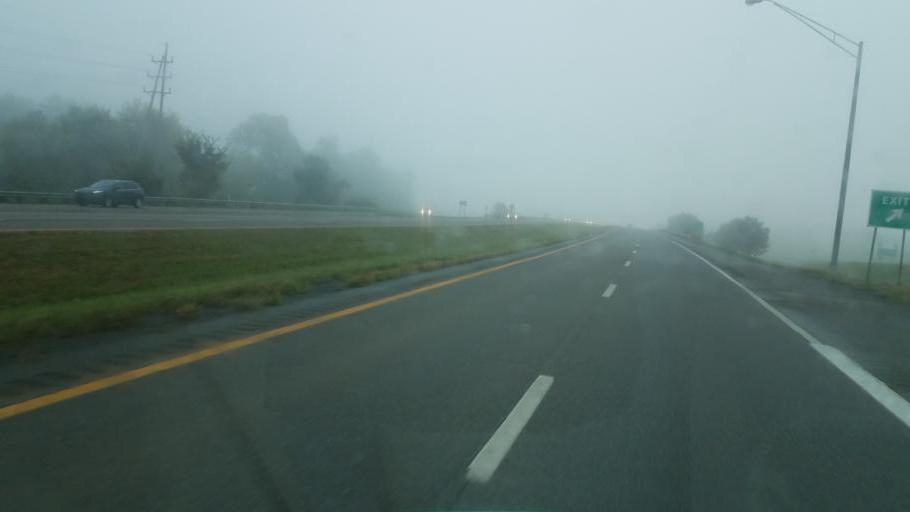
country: US
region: Ohio
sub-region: Tuscarawas County
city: New Philadelphia
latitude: 40.4804
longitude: -81.4524
